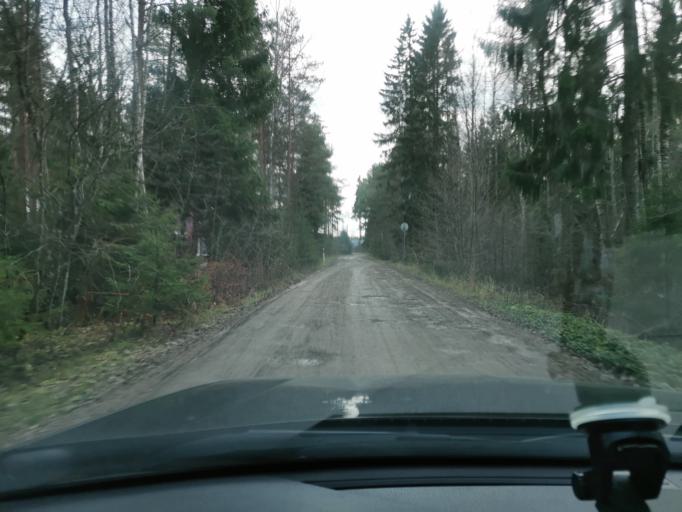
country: EE
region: Ida-Virumaa
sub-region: Sillamaee linn
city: Sillamae
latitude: 59.2551
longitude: 27.9134
